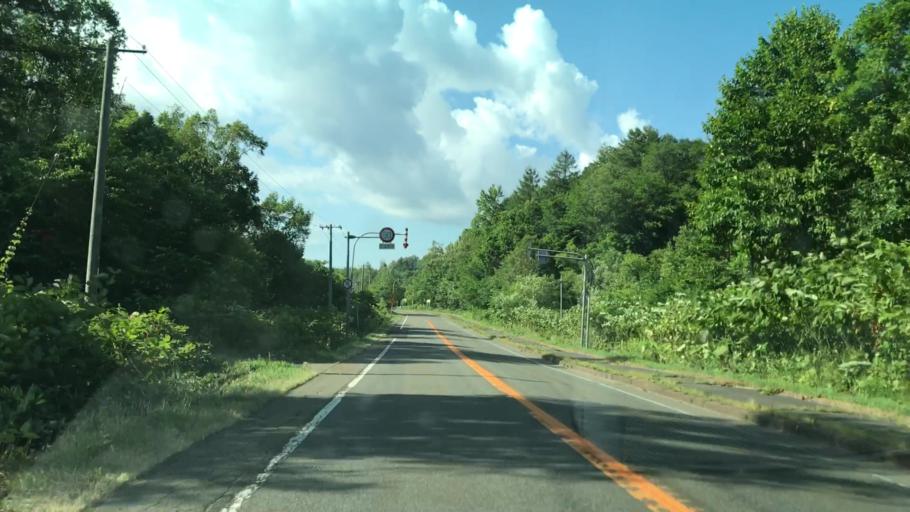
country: JP
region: Hokkaido
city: Shimo-furano
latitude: 42.8942
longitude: 142.4304
